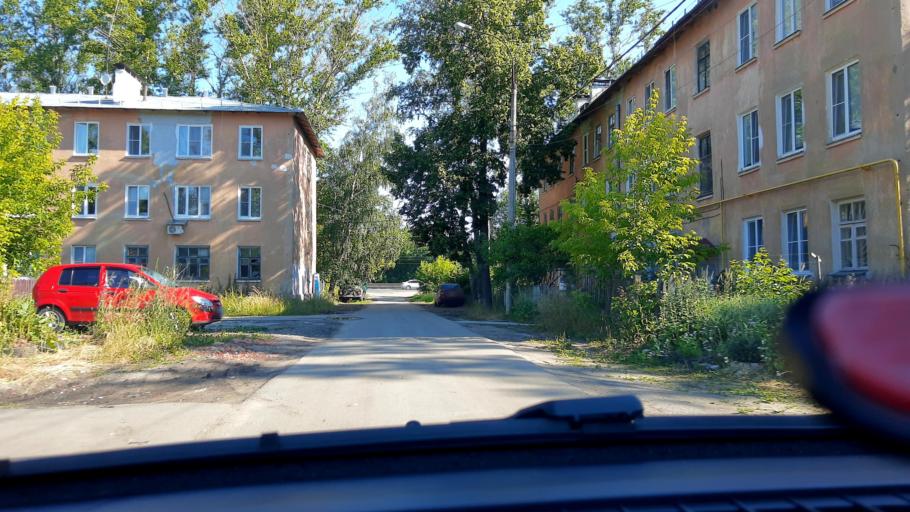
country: RU
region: Nizjnij Novgorod
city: Gorbatovka
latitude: 56.3100
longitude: 43.8048
